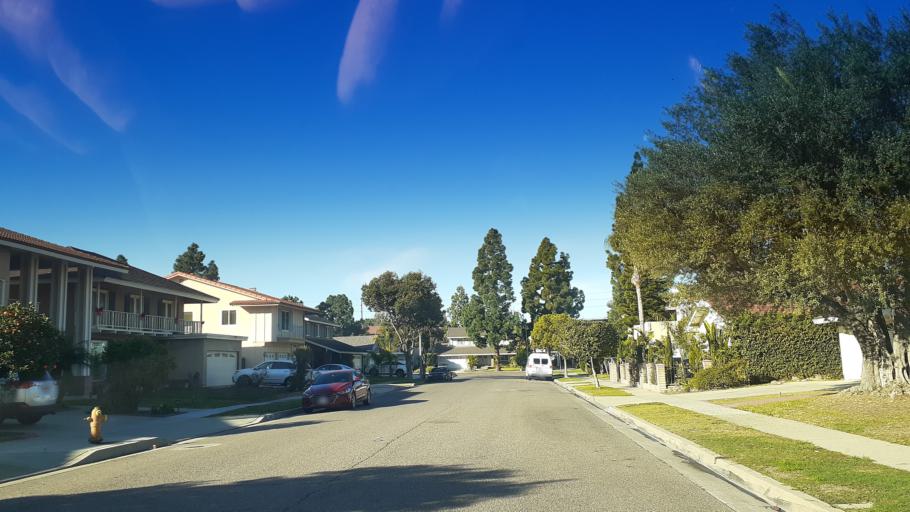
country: US
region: California
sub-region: Los Angeles County
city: Cerritos
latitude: 33.8481
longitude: -118.0705
